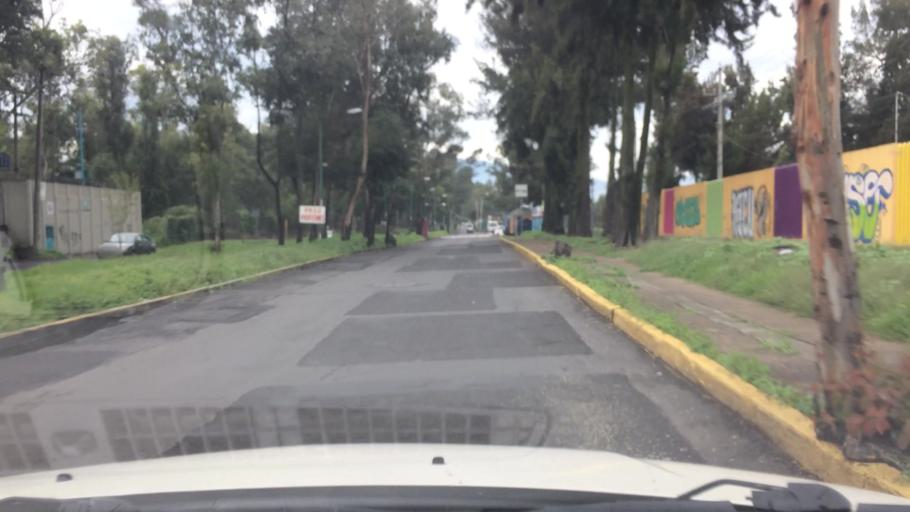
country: MX
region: Mexico City
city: Iztapalapa
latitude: 19.3161
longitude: -99.0998
